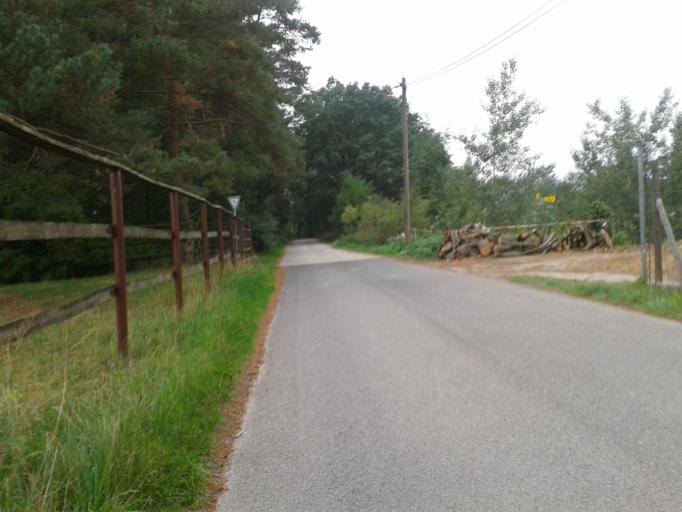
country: DE
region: Bavaria
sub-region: Upper Franconia
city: Gundelsheim
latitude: 49.9272
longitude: 10.9029
